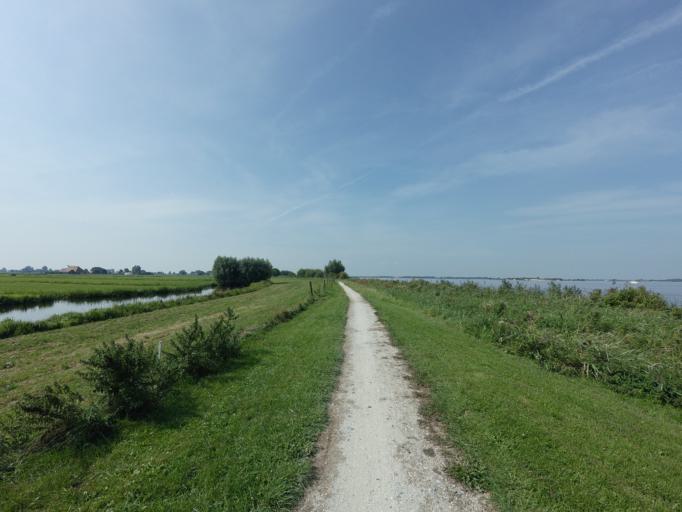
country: NL
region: Friesland
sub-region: Gemeente Lemsterland
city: Echtenerbrug
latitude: 52.8772
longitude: 5.7979
